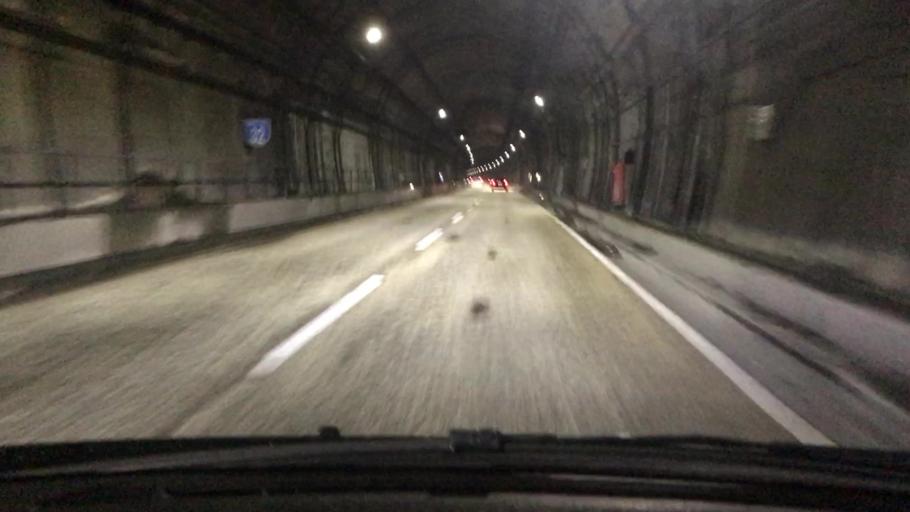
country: JP
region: Hyogo
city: Kobe
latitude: 34.7248
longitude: 135.1833
